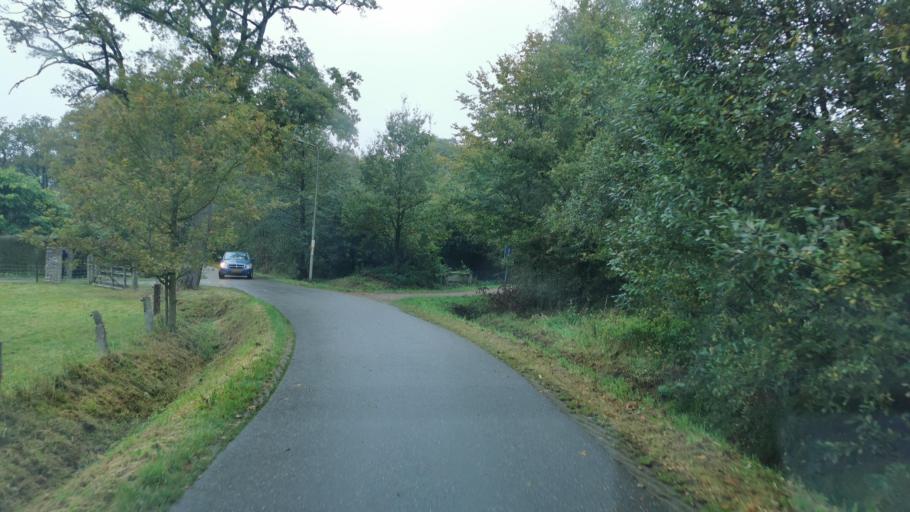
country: NL
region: Overijssel
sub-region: Gemeente Oldenzaal
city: Oldenzaal
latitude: 52.3087
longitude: 6.9501
